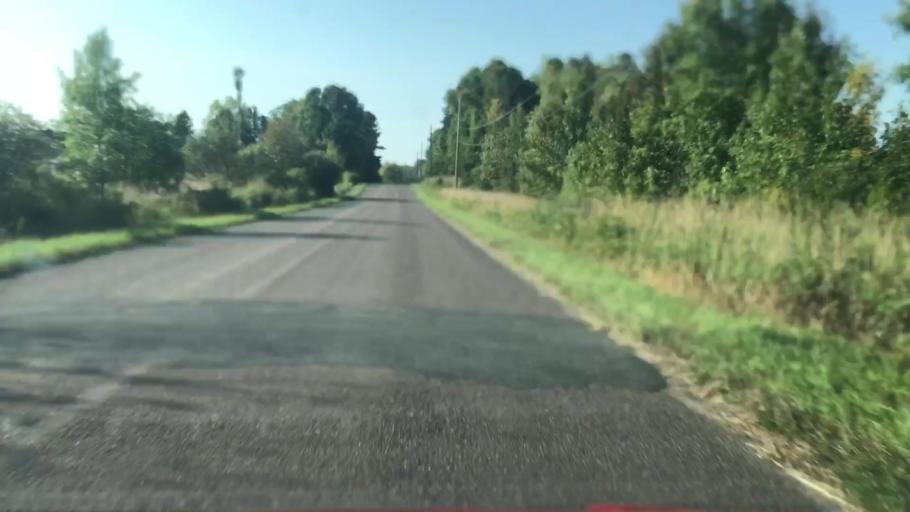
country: US
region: Michigan
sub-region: Chippewa County
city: Sault Ste. Marie
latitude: 46.2879
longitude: -84.0598
